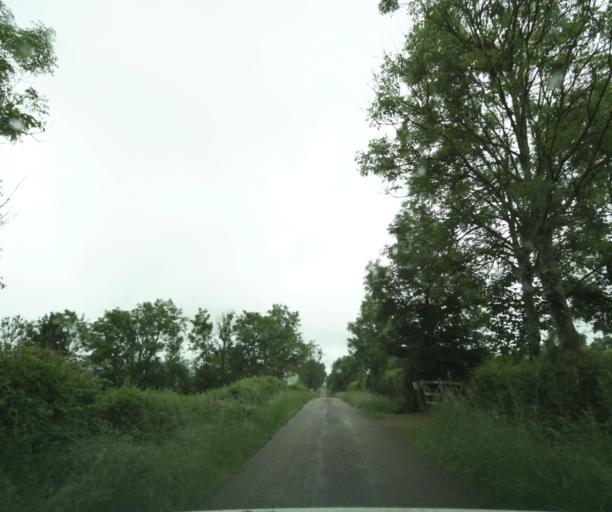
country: FR
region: Bourgogne
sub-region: Departement de Saone-et-Loire
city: Charolles
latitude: 46.4437
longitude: 4.3247
